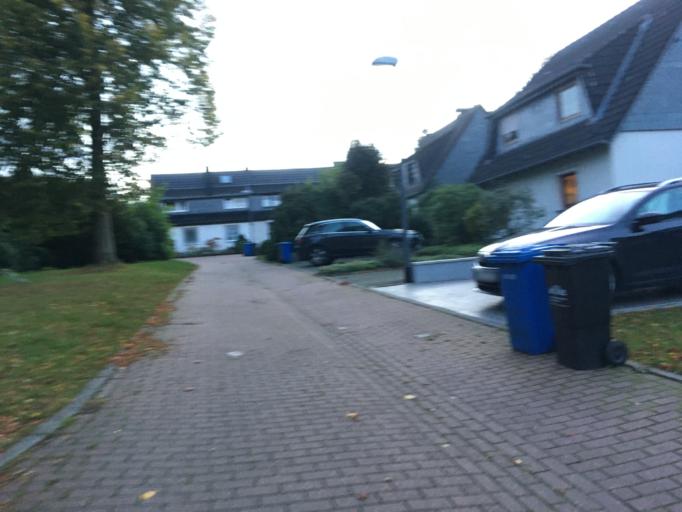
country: DE
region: North Rhine-Westphalia
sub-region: Regierungsbezirk Munster
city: Bottrop
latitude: 51.4783
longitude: 6.9349
